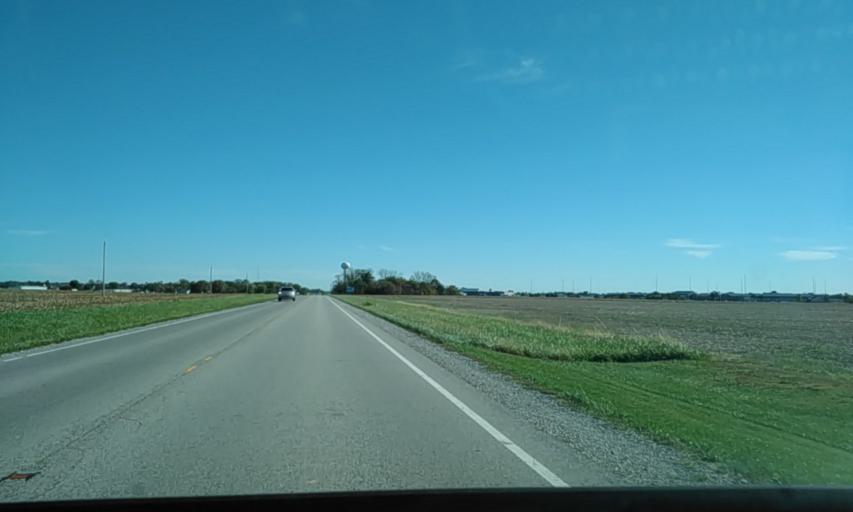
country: US
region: Illinois
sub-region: Bond County
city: Greenville
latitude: 38.8662
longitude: -89.4226
